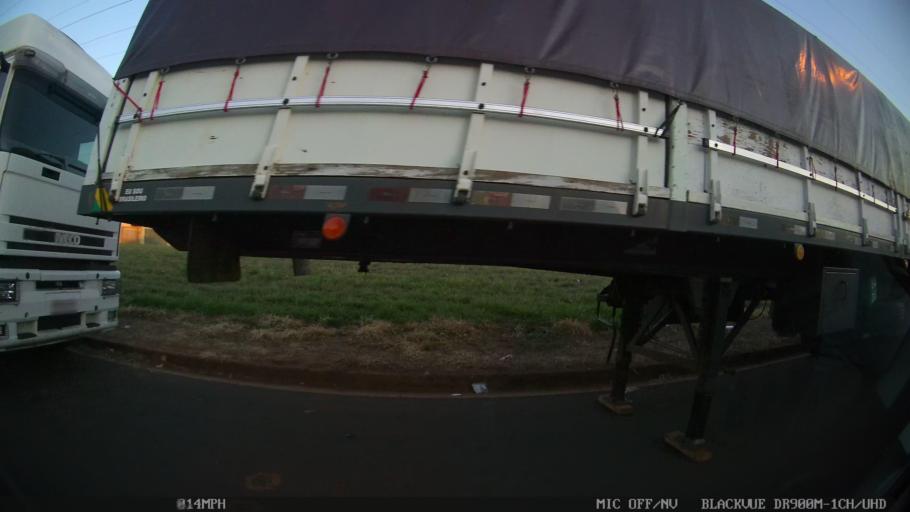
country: BR
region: Sao Paulo
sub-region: Sao Jose Do Rio Preto
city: Sao Jose do Rio Preto
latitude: -20.7971
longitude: -49.3495
